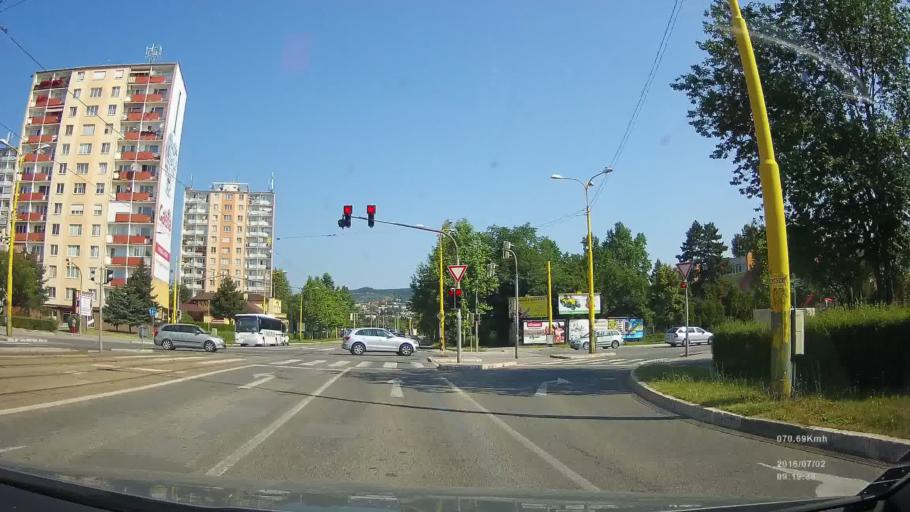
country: SK
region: Kosicky
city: Kosice
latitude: 48.7375
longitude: 21.2393
